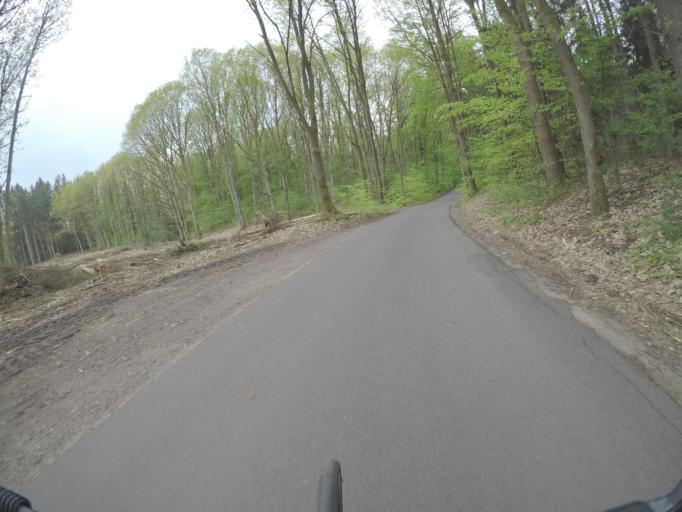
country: DE
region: Brandenburg
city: Marienwerder
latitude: 52.8976
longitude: 13.6569
